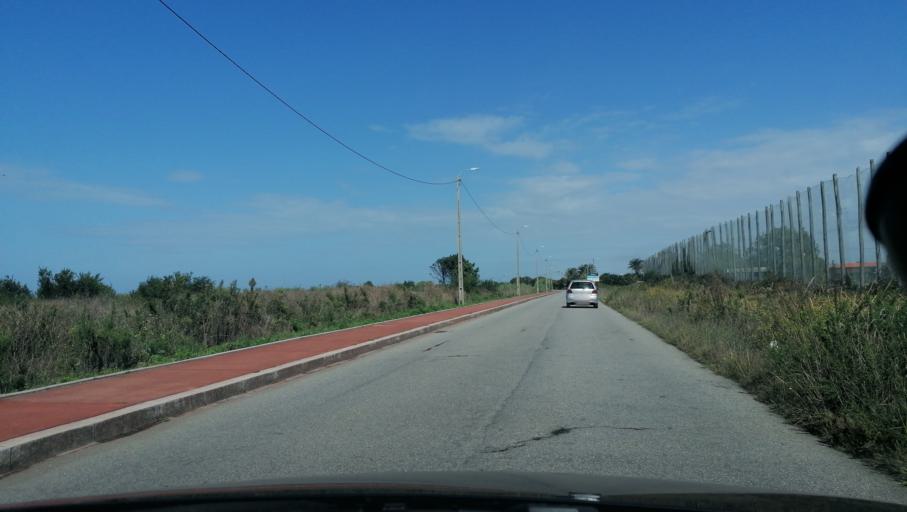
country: PT
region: Aveiro
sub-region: Espinho
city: Silvalde
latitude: 40.9824
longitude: -8.6424
